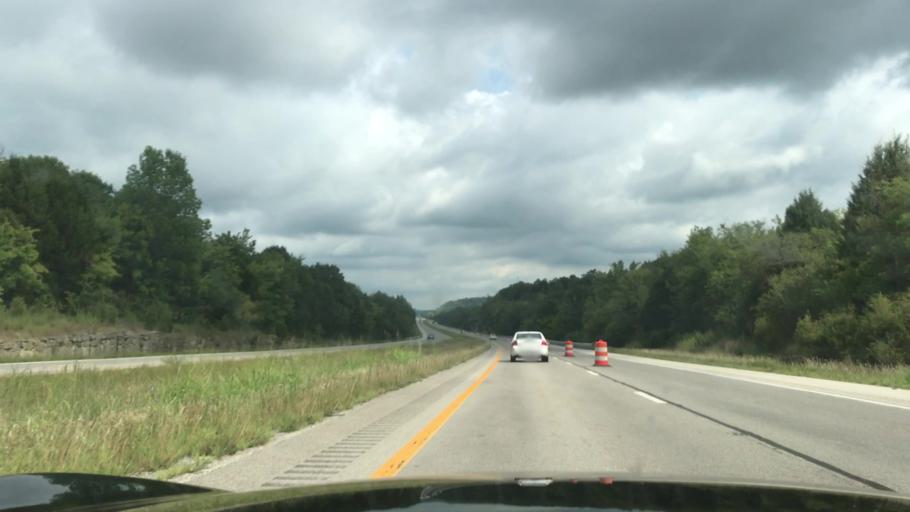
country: US
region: Kentucky
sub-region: Butler County
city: Morgantown
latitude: 37.1207
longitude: -86.6424
